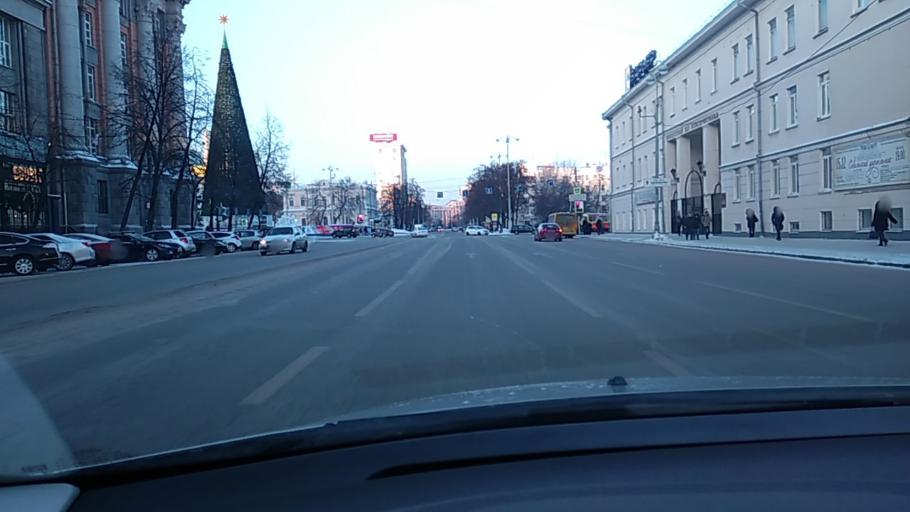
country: RU
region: Sverdlovsk
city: Yekaterinburg
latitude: 56.8368
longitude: 60.5992
